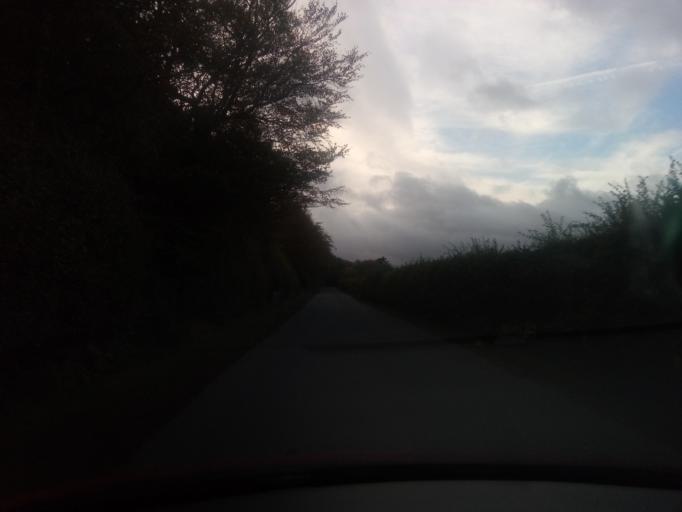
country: GB
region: Scotland
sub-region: The Scottish Borders
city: Jedburgh
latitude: 55.3867
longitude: -2.6432
